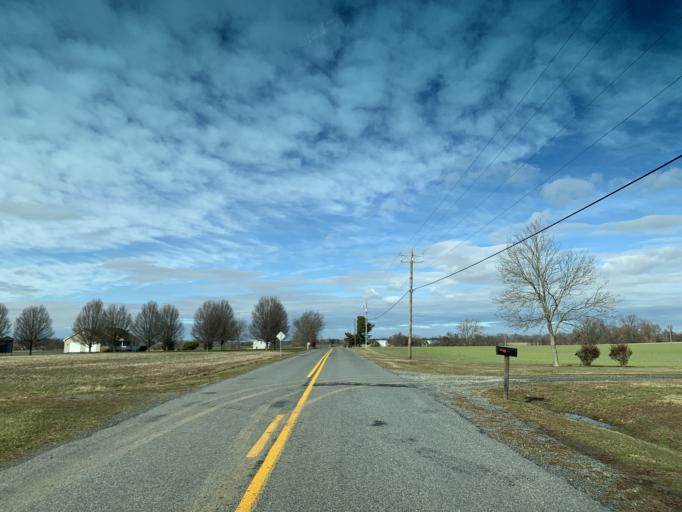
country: US
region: Maryland
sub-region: Kent County
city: Chestertown
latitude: 39.3392
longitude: -76.0493
